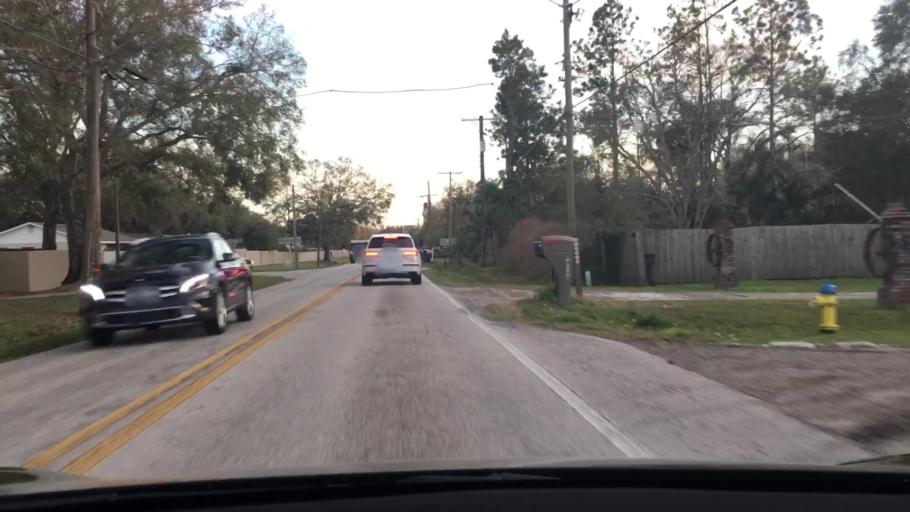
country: US
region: Florida
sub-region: Hillsborough County
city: Greater Northdale
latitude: 28.0900
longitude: -82.5399
